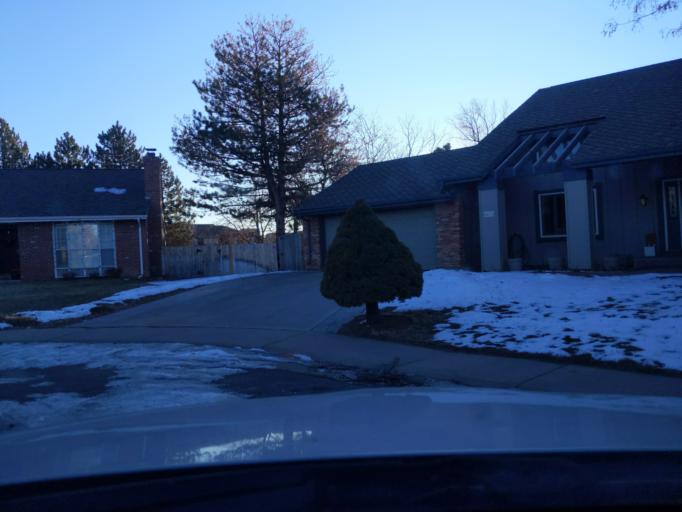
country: US
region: Colorado
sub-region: Arapahoe County
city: Centennial
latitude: 39.5701
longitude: -104.8866
